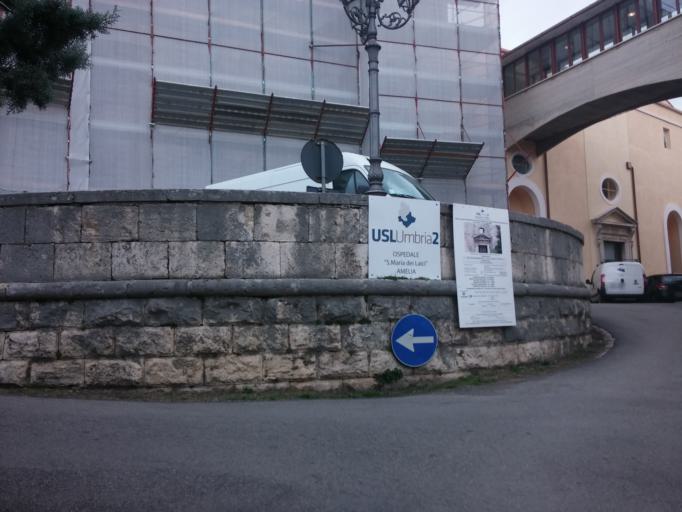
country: IT
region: Umbria
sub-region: Provincia di Terni
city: Amelia
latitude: 42.5591
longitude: 12.4122
